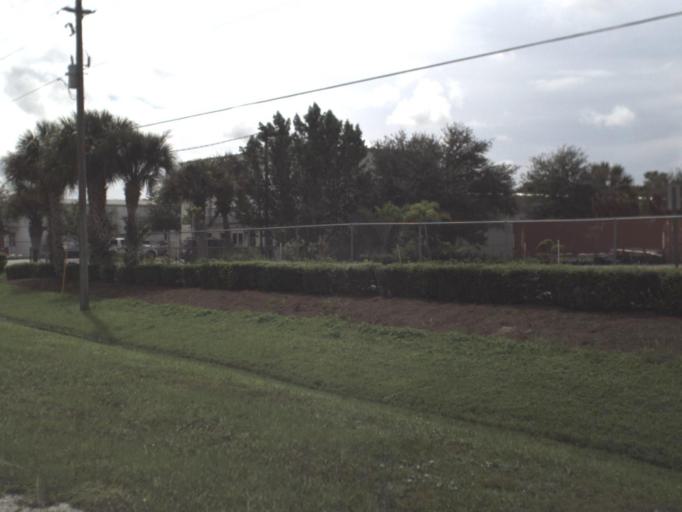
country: US
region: Florida
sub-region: Lee County
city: Pine Manor
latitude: 26.5750
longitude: -81.8532
